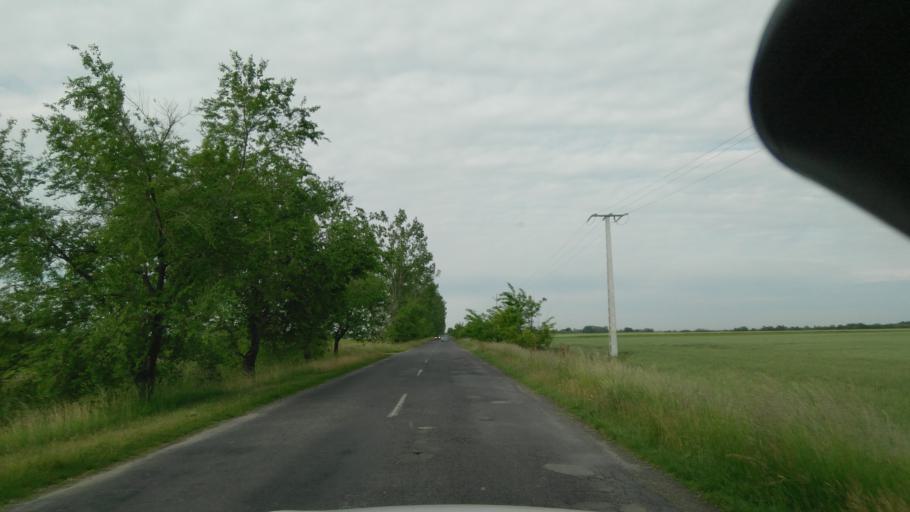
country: HU
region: Bekes
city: Ketegyhaza
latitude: 46.5608
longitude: 21.2015
